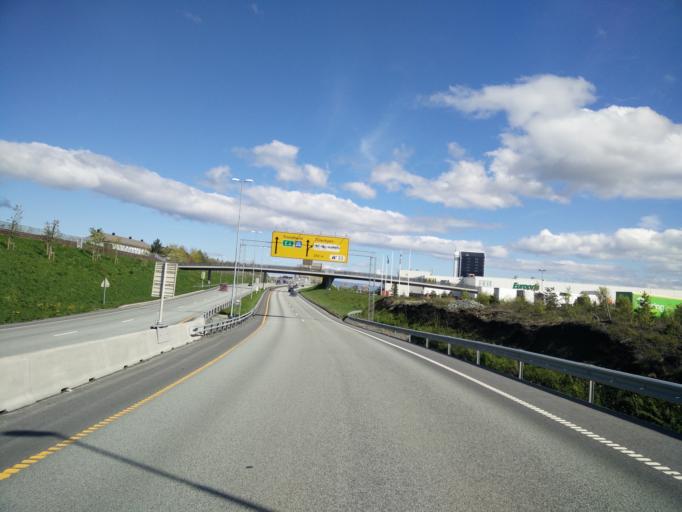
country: NO
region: Sor-Trondelag
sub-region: Trondheim
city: Trondheim
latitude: 63.3547
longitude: 10.3709
